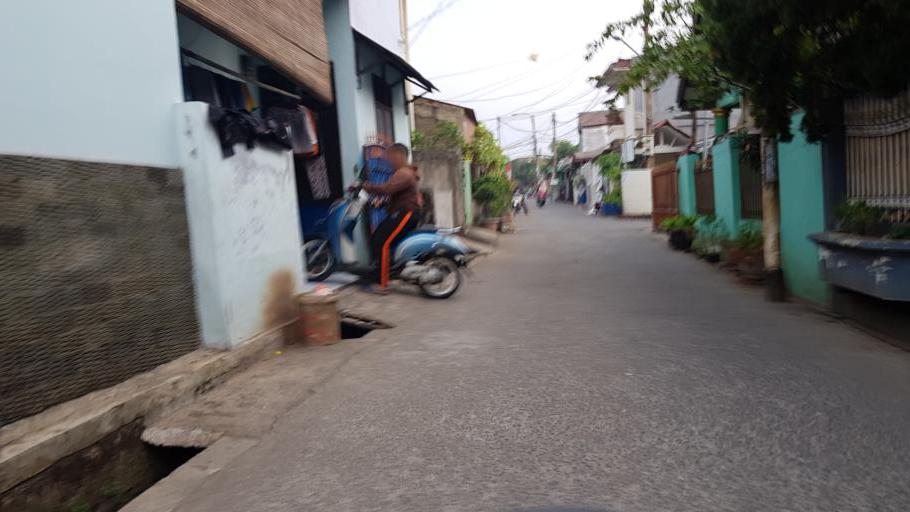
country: ID
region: West Java
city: Bekasi
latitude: -6.2774
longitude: 106.9306
